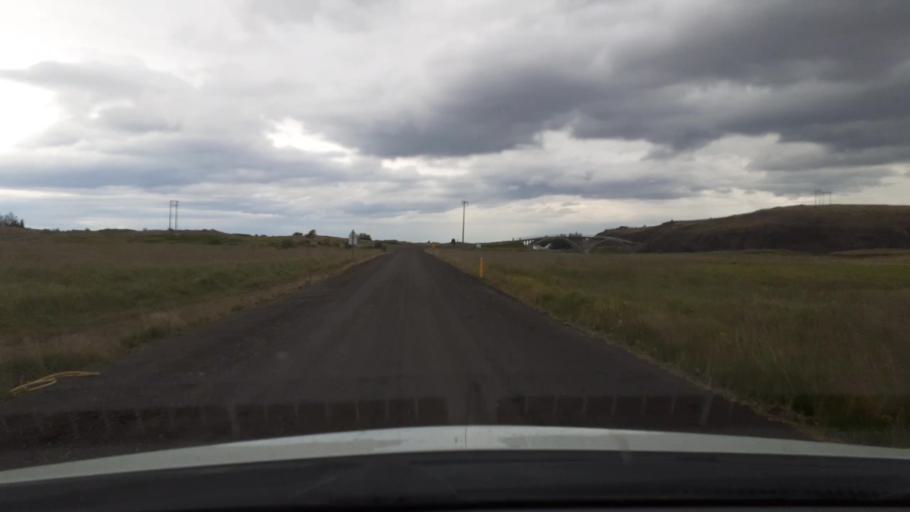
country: IS
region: West
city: Borgarnes
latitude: 64.6037
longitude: -21.7020
